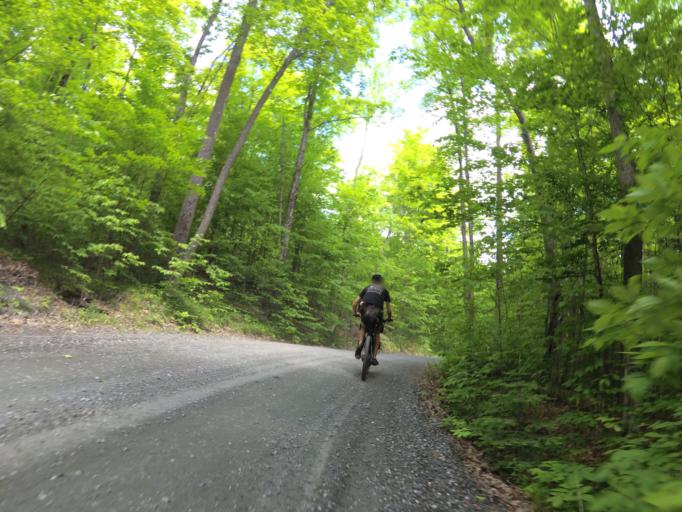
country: CA
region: Ontario
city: Renfrew
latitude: 45.0681
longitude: -76.8002
